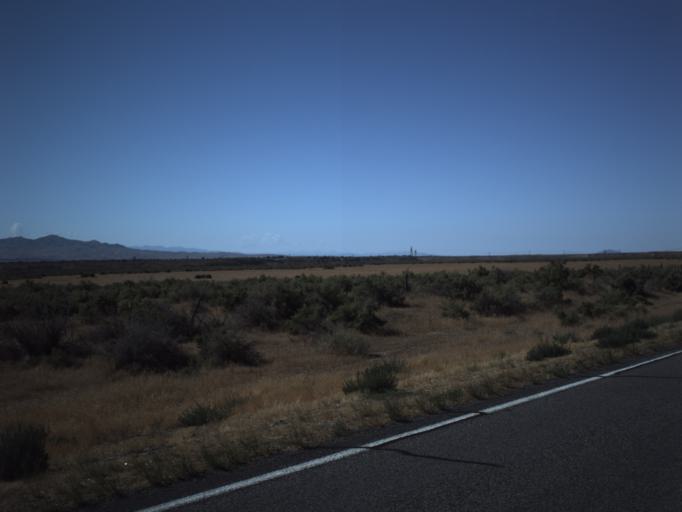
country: US
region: Utah
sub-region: Millard County
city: Delta
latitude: 39.5040
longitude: -112.3883
